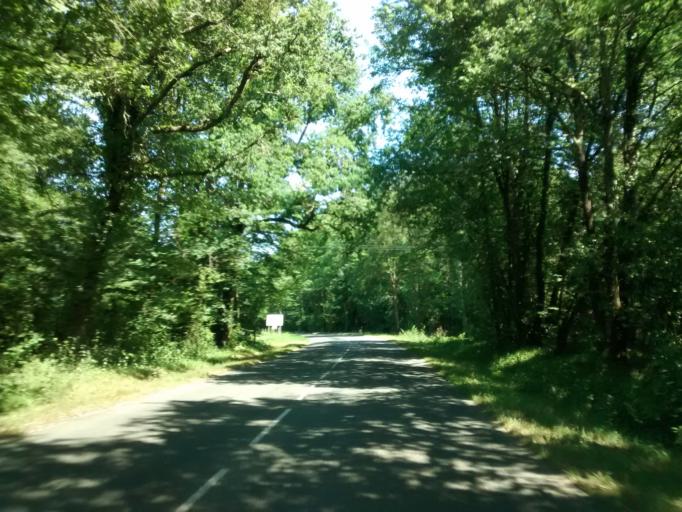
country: FR
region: Aquitaine
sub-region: Departement de la Gironde
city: Lussac
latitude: 44.9437
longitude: -0.1142
